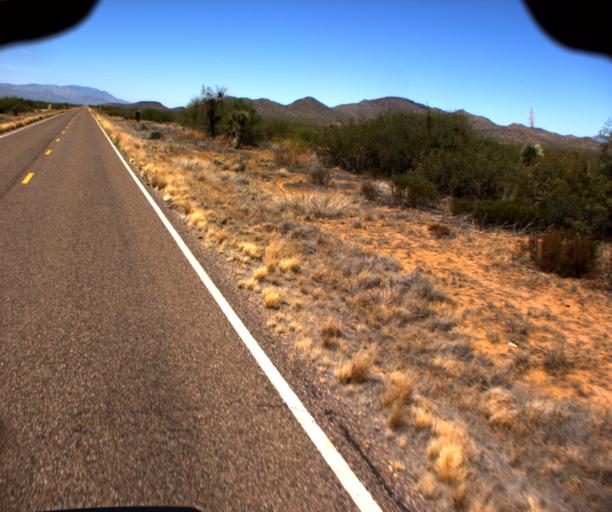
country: US
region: Arizona
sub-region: Yavapai County
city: Congress
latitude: 34.0510
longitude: -113.0577
